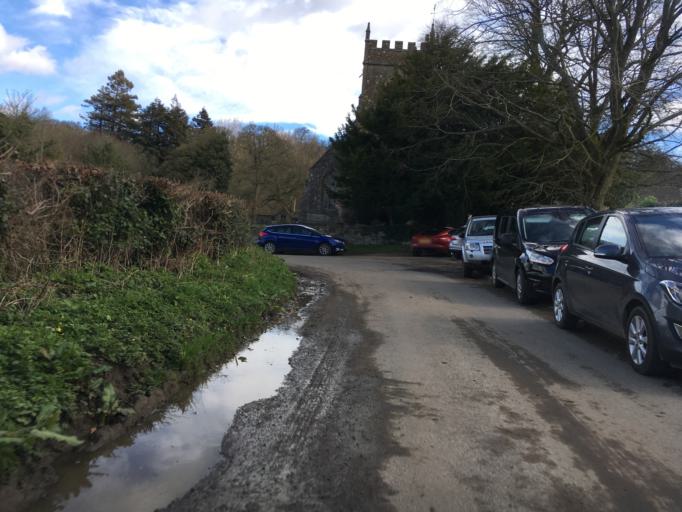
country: GB
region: England
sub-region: South Gloucestershire
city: Horton
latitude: 51.5636
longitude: -2.3398
